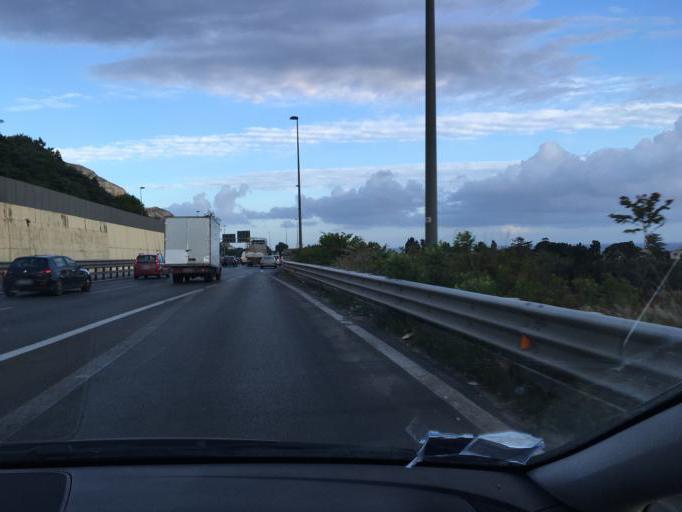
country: IT
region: Sicily
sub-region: Palermo
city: Isola delle Femmine
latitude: 38.1928
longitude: 13.2802
